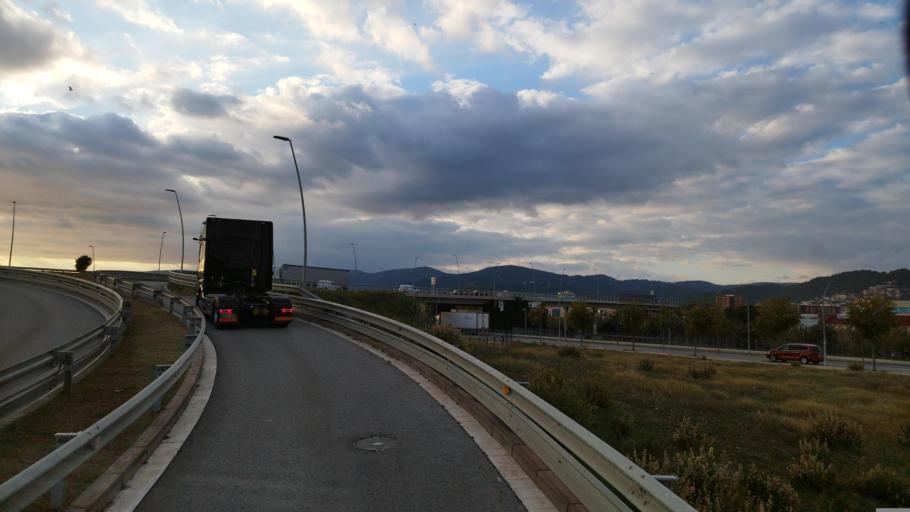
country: ES
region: Catalonia
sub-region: Provincia de Barcelona
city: Viladecans
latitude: 41.3065
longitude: 2.0231
